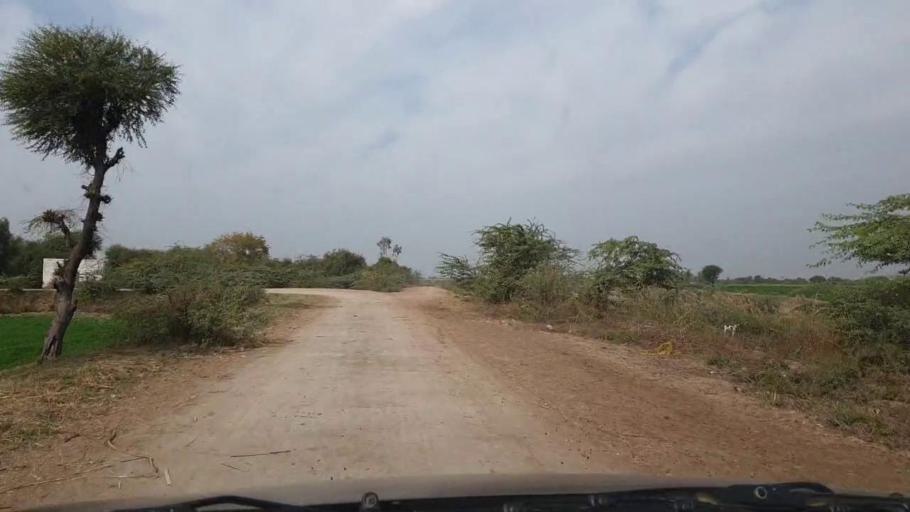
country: PK
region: Sindh
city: Sanghar
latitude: 26.0914
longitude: 68.8950
